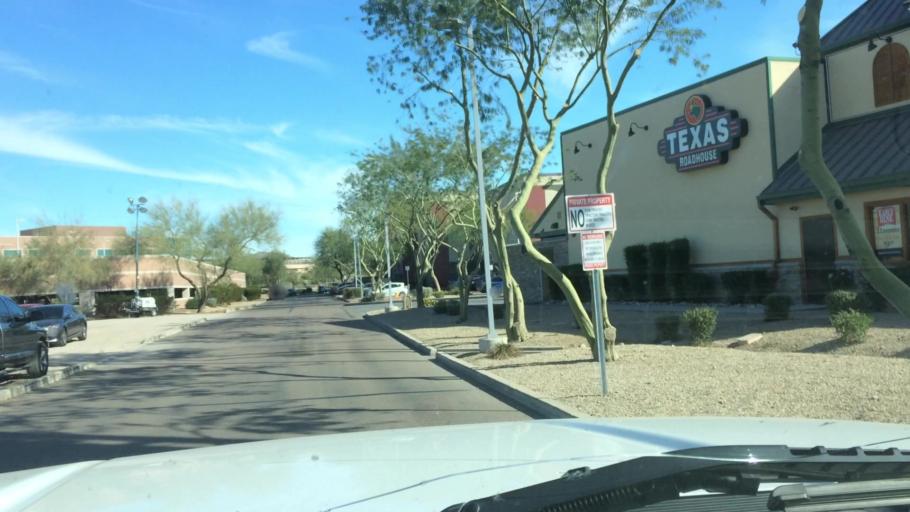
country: US
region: Arizona
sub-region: Maricopa County
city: Anthem
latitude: 33.7150
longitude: -112.1162
